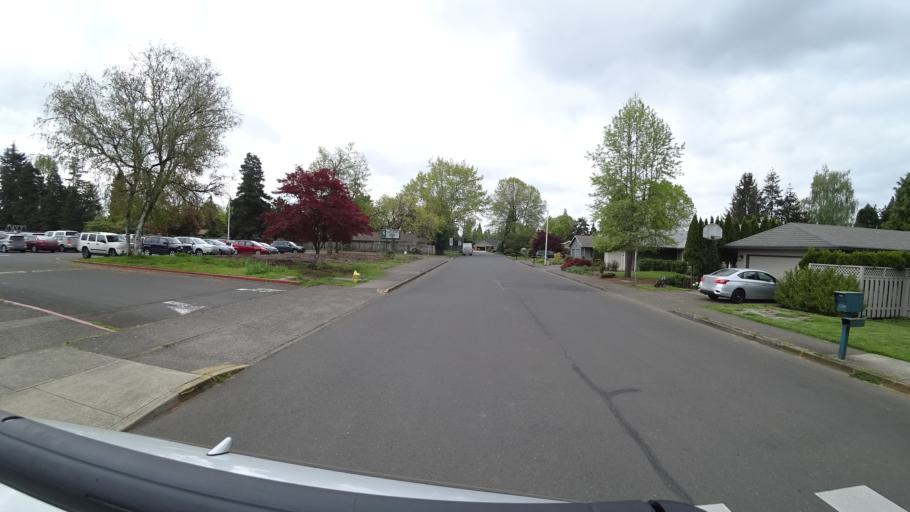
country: US
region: Oregon
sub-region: Washington County
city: Hillsboro
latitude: 45.5338
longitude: -122.9729
